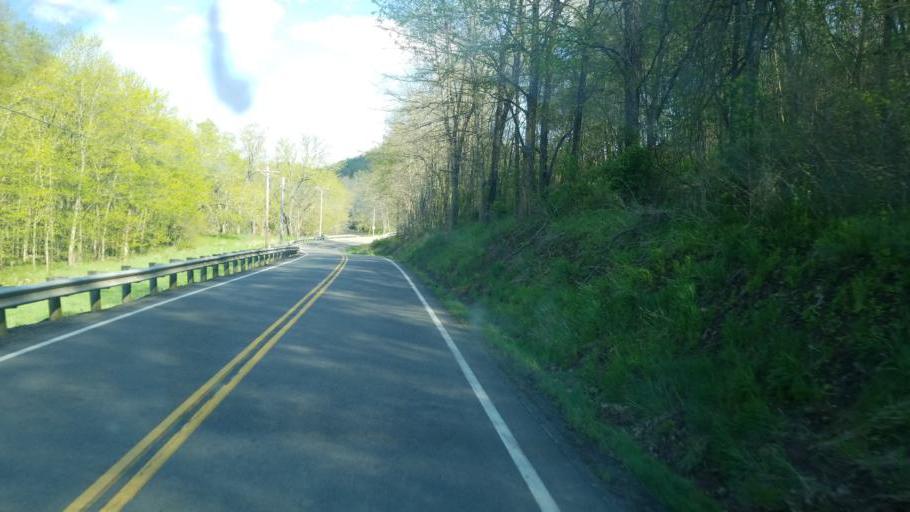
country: US
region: Ohio
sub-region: Coshocton County
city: Coshocton
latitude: 40.3595
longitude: -81.9757
